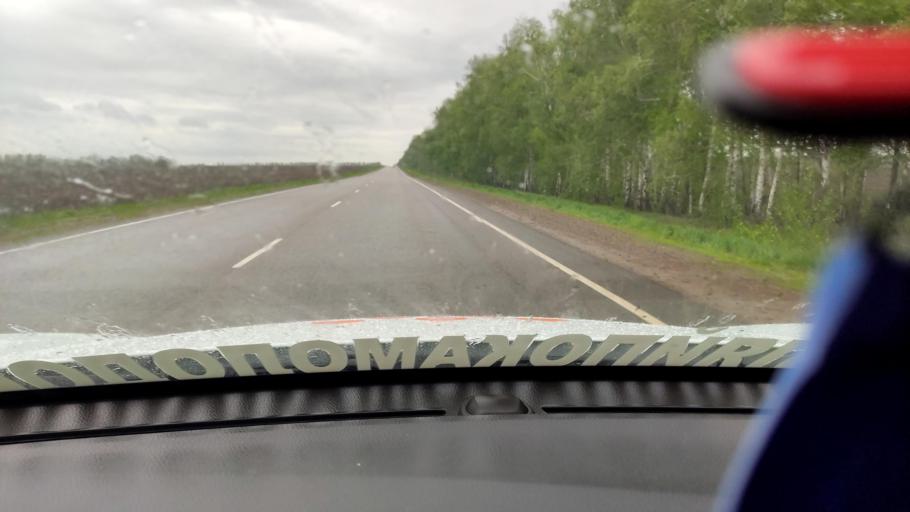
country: RU
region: Voronezj
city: Sredniy Ikorets
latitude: 51.0414
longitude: 39.6842
